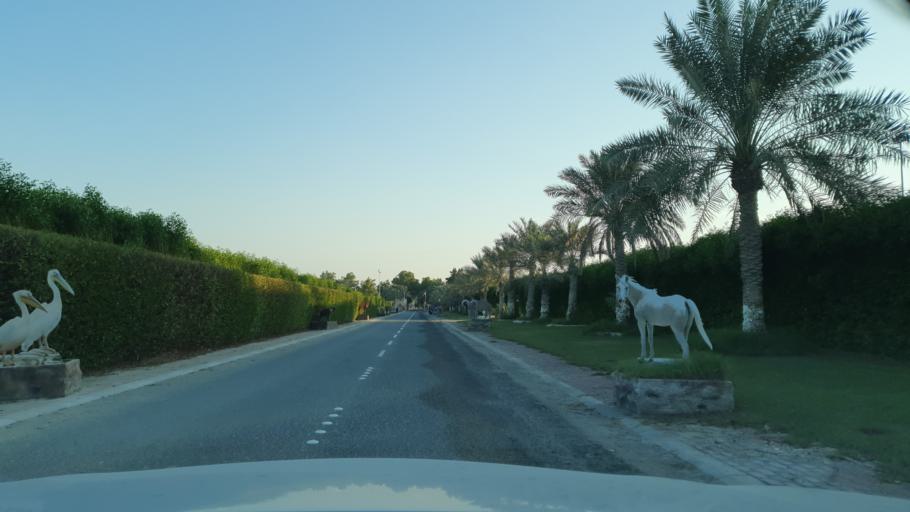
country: BH
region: Central Governorate
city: Dar Kulayb
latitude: 26.0179
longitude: 50.4940
